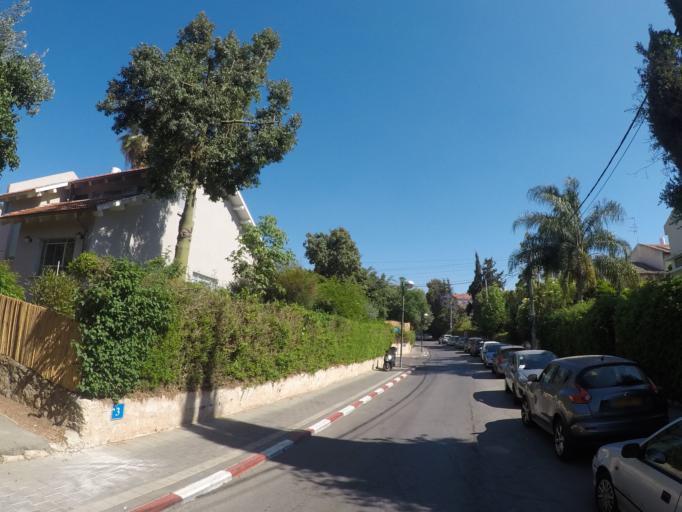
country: IL
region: Tel Aviv
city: Ramat Gan
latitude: 32.1088
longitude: 34.7996
